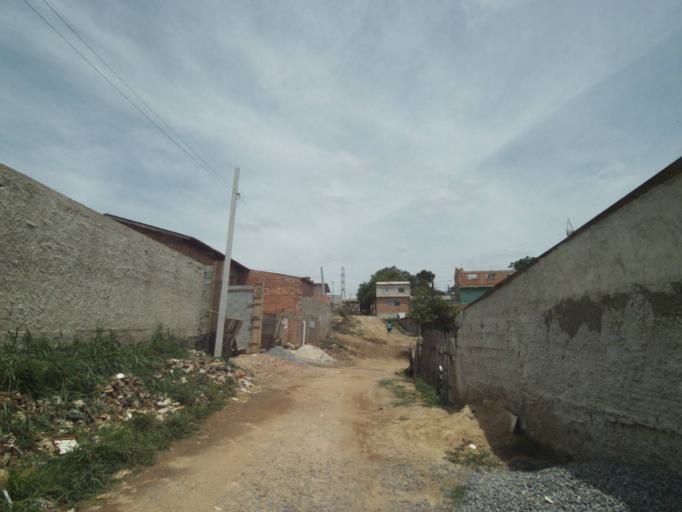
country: BR
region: Parana
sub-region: Curitiba
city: Curitiba
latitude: -25.4994
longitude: -49.3399
